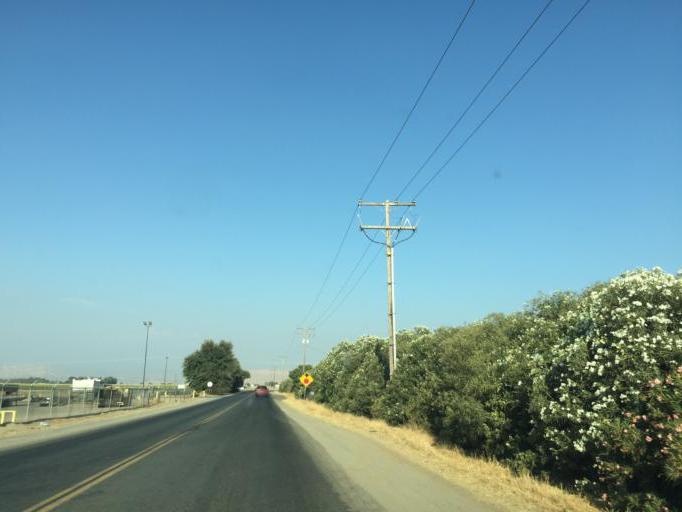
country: US
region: California
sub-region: Tulare County
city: Cutler
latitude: 36.4578
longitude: -119.2982
